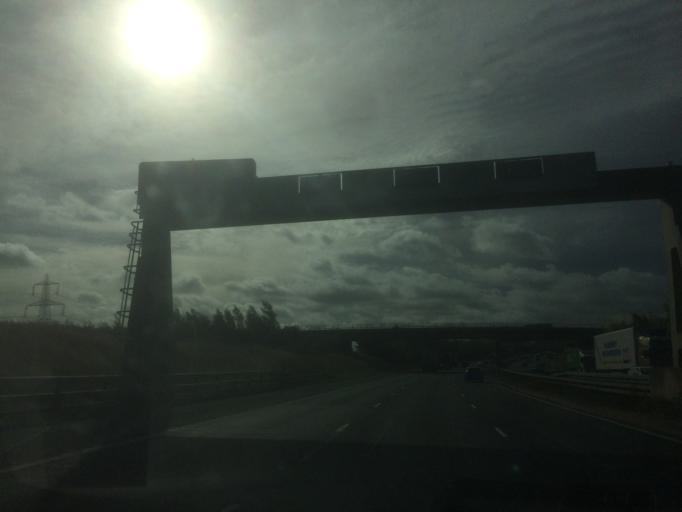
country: GB
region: England
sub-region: North Yorkshire
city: Byram
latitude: 53.7470
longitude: -1.2733
